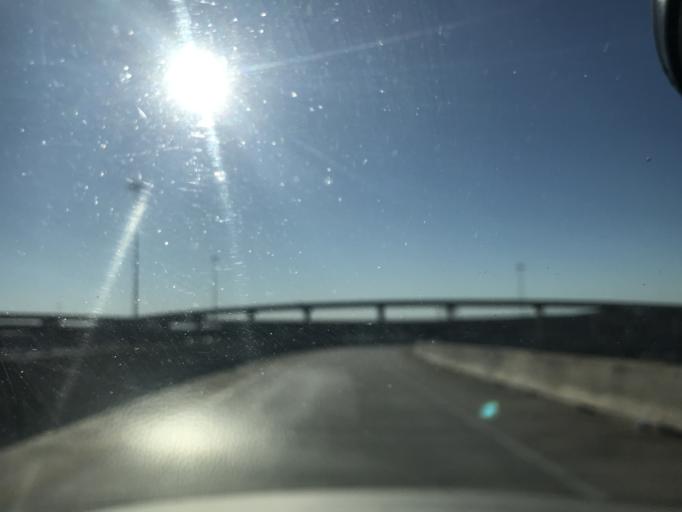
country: US
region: Texas
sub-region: Denton County
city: Lewisville
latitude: 33.0017
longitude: -96.9581
